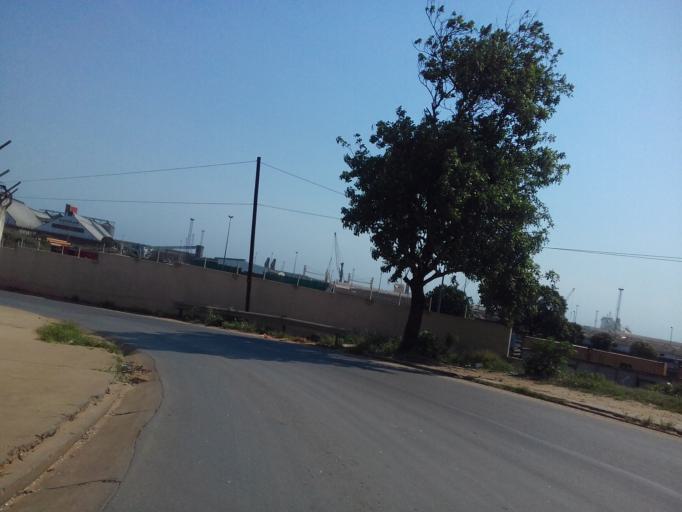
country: MZ
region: Maputo City
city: Maputo
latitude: -25.9580
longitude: 32.5541
